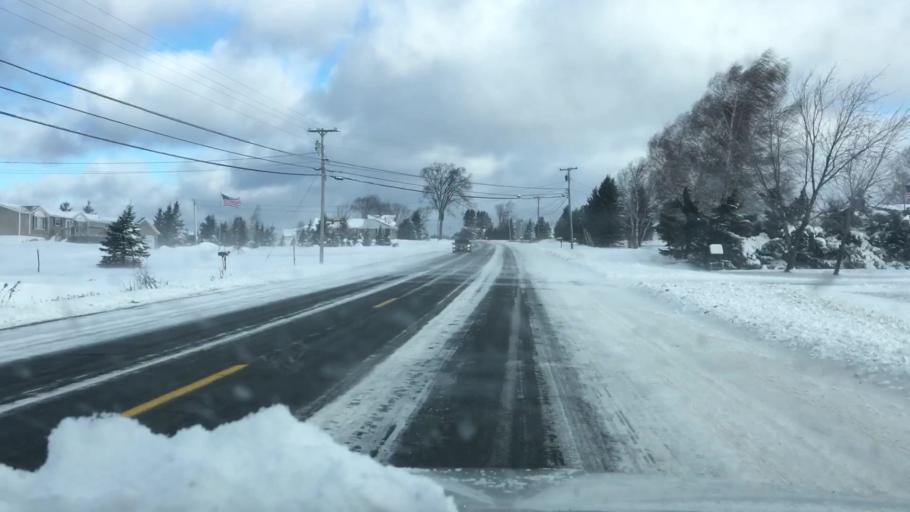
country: US
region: Maine
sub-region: Aroostook County
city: Caribou
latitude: 46.8994
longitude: -68.0154
